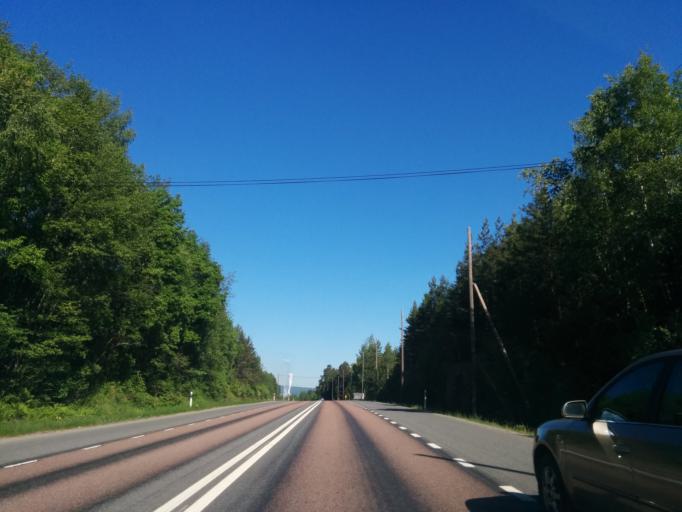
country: SE
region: Vaesternorrland
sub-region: Kramfors Kommun
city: Kramfors
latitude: 62.9529
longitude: 17.7681
